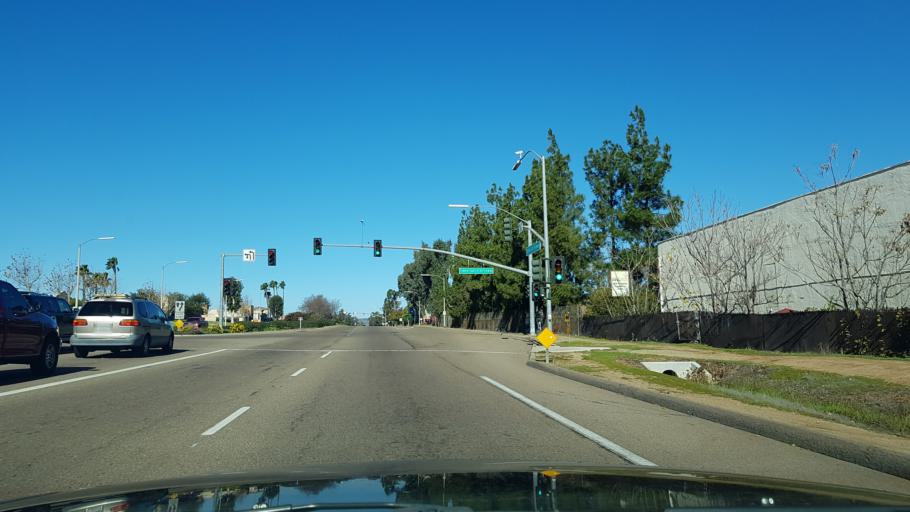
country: US
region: California
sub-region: San Diego County
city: Escondido
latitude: 33.1003
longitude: -117.0734
